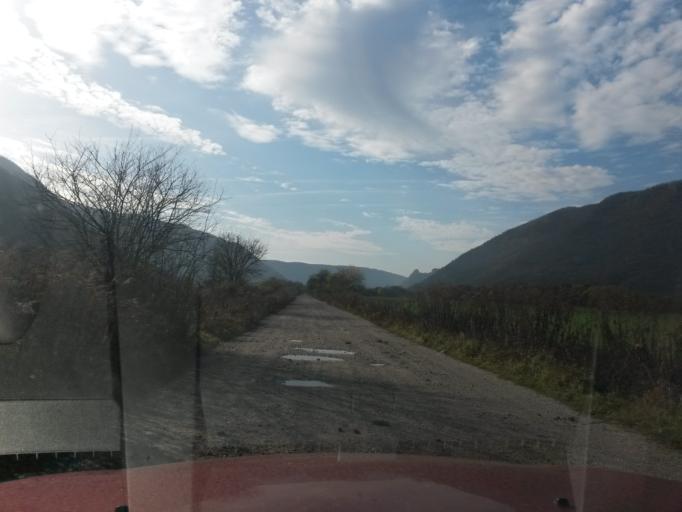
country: SK
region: Kosicky
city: Roznava
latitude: 48.6124
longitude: 20.4859
